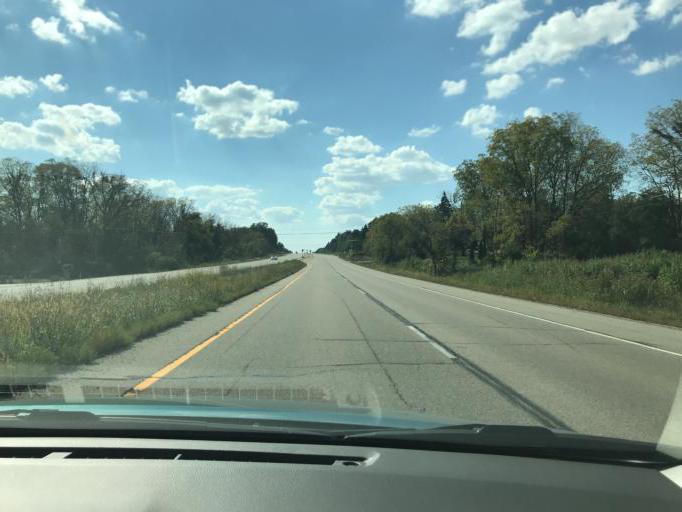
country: US
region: Wisconsin
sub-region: Walworth County
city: Como
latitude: 42.5875
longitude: -88.4772
